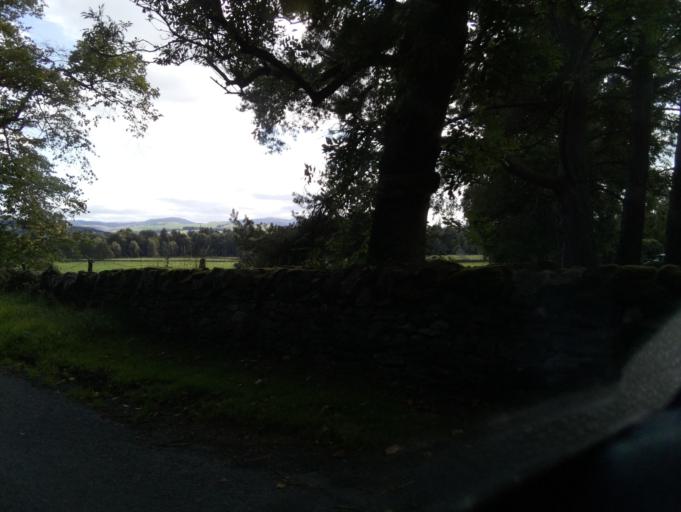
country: GB
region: Scotland
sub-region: The Scottish Borders
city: West Linton
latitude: 55.7396
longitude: -3.3348
